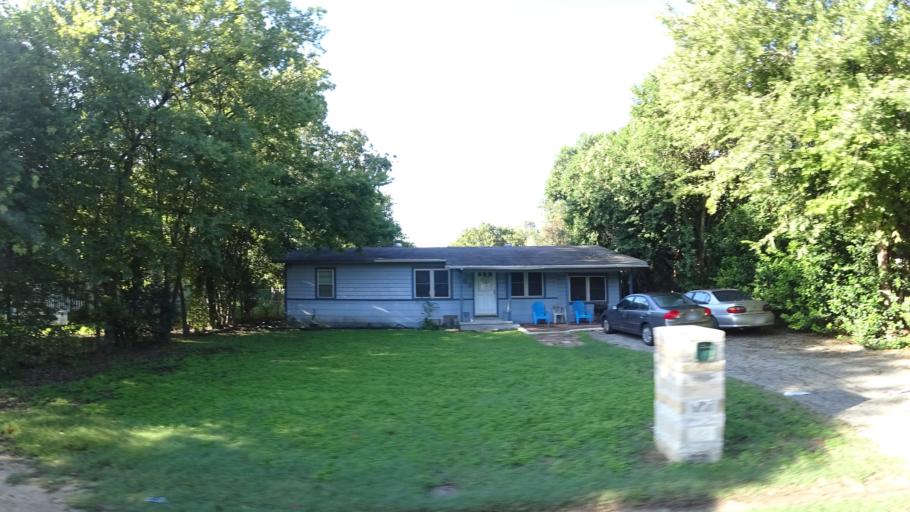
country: US
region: Texas
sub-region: Travis County
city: Wells Branch
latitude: 30.3580
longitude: -97.6922
